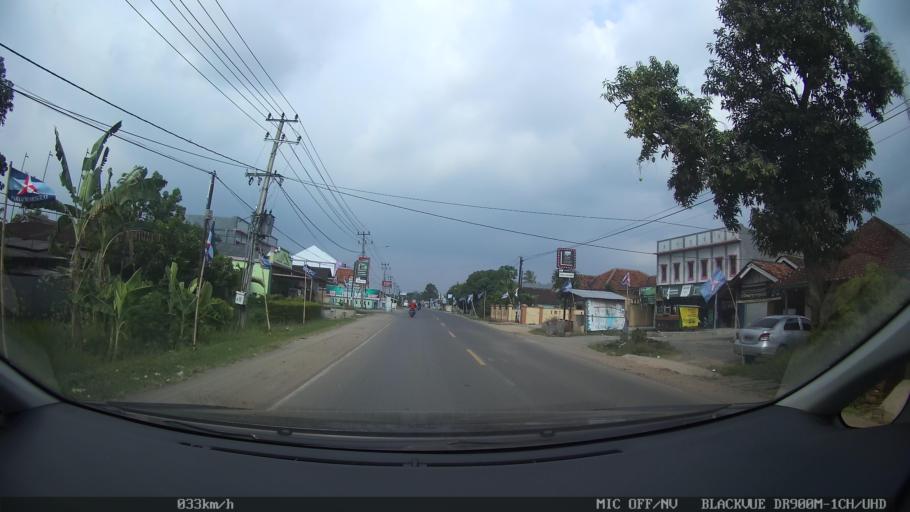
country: ID
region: Lampung
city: Gadingrejo
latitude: -5.3777
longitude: 105.0339
